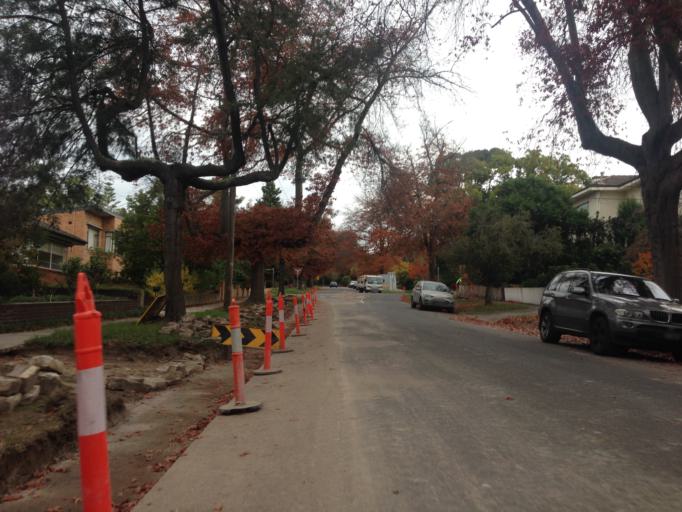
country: AU
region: Victoria
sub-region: Boroondara
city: Kew East
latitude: -37.7890
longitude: 145.0693
